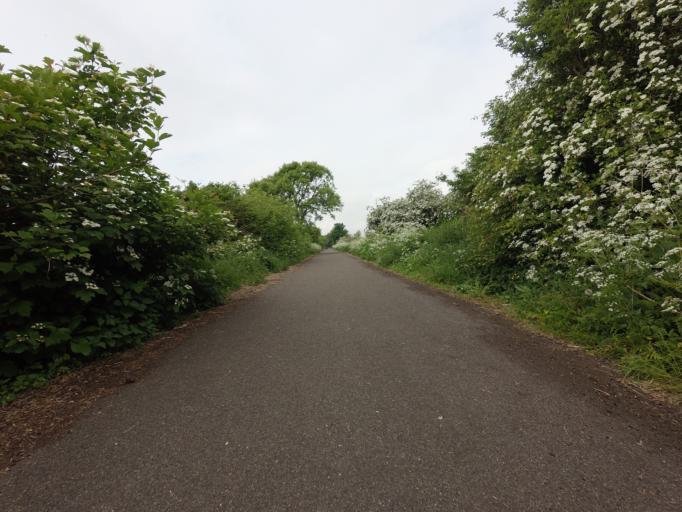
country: GB
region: Scotland
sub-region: Fife
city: Townhill
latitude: 56.0882
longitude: -3.4433
